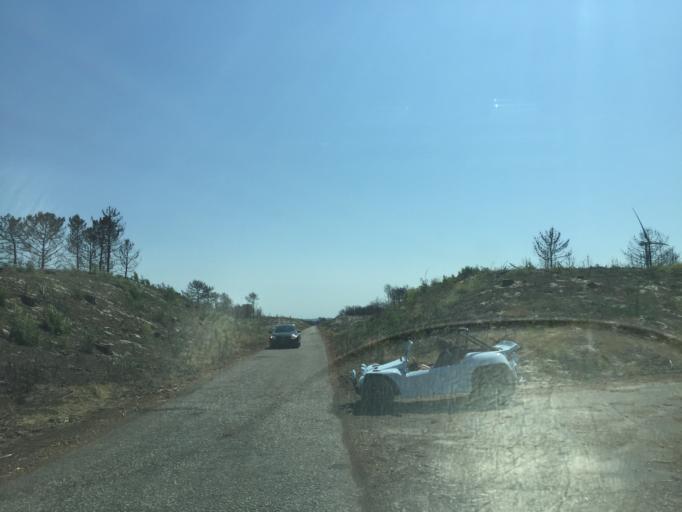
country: PT
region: Coimbra
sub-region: Mira
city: Mira
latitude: 40.3192
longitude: -8.8108
